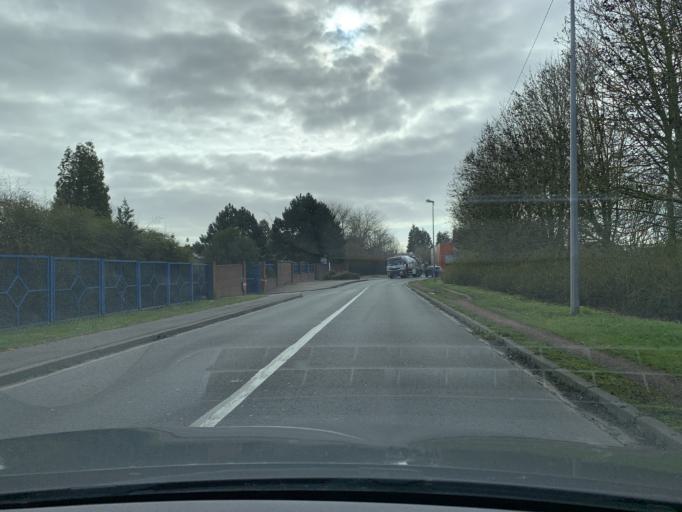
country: FR
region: Nord-Pas-de-Calais
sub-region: Departement du Nord
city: Waziers
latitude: 50.3930
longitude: 3.1049
